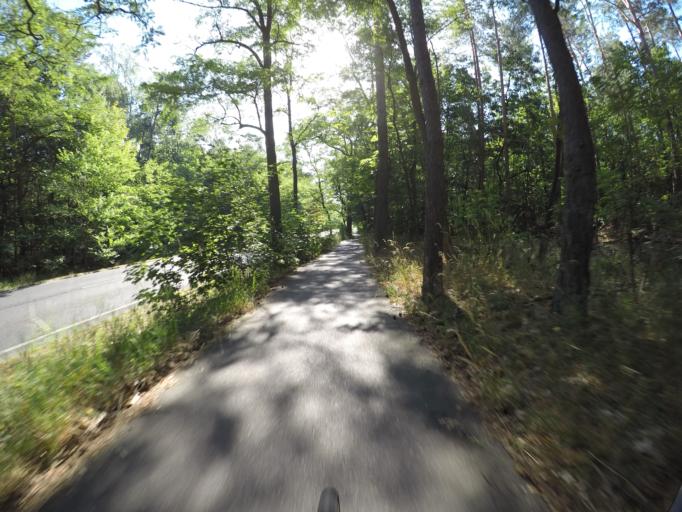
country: DE
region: Berlin
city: Schmockwitz
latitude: 52.3710
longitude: 13.6768
